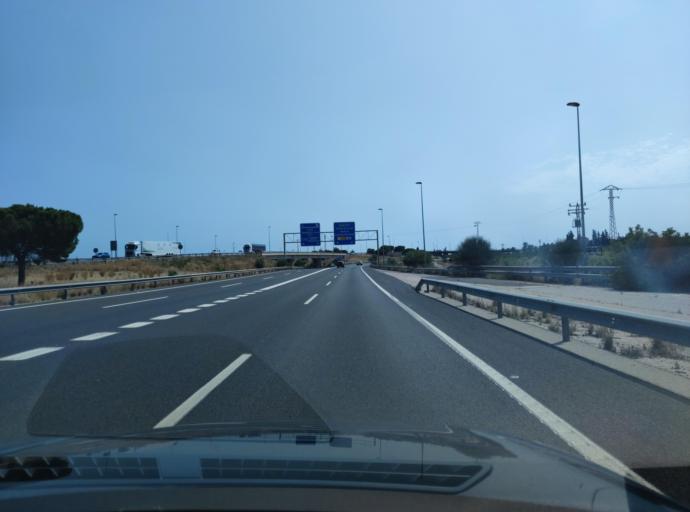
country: ES
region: Valencia
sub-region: Provincia de Valencia
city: Pucol
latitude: 39.6360
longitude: -0.3036
